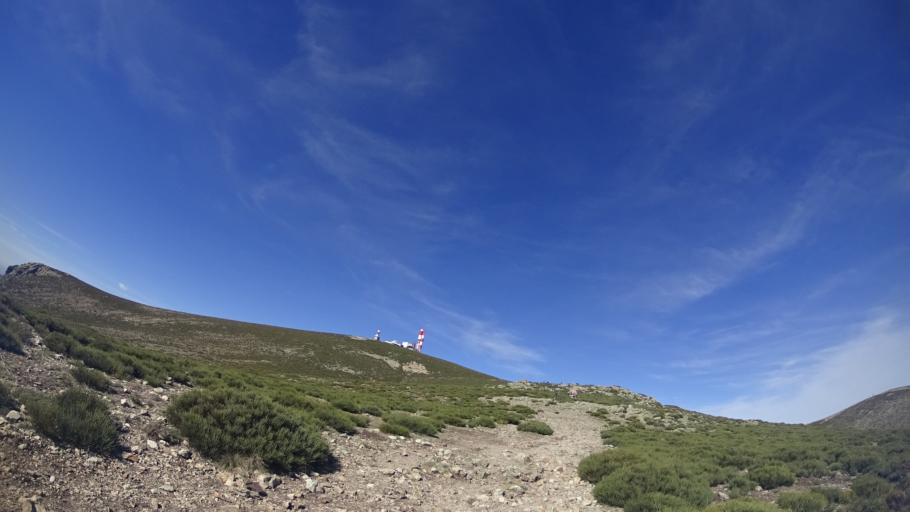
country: ES
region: Madrid
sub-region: Provincia de Madrid
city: Becerril de la Sierra
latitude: 40.7792
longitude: -3.9741
